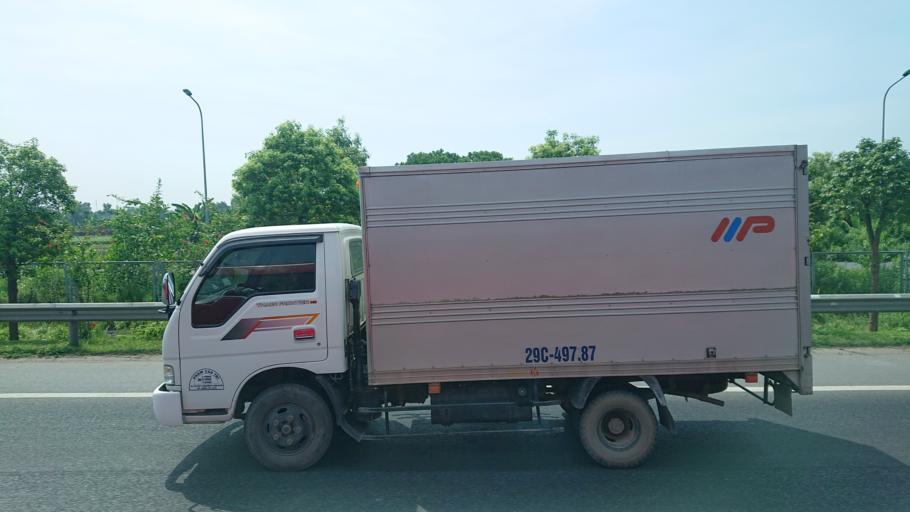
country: VN
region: Ha Noi
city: Dong Anh
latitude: 21.1931
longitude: 105.8342
